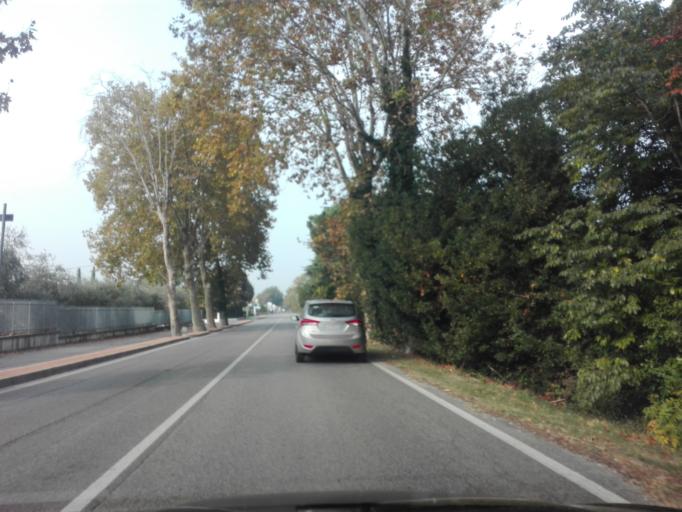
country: IT
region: Veneto
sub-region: Provincia di Verona
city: Peschiera del Garda
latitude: 45.4540
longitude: 10.6539
